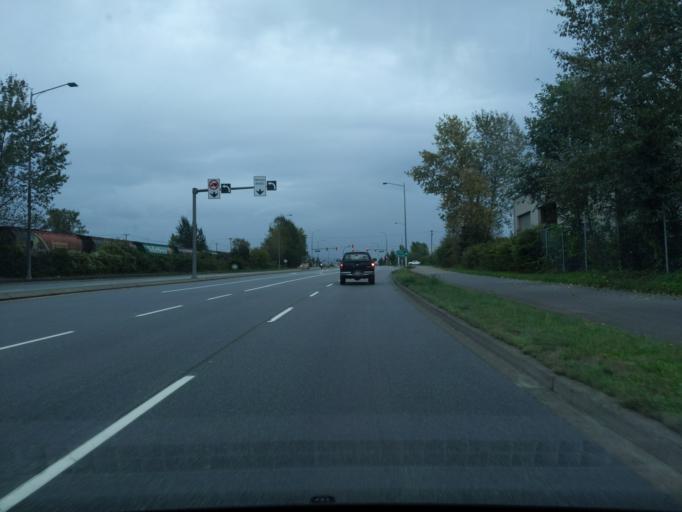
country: CA
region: British Columbia
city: Pitt Meadows
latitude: 49.1809
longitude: -122.6933
